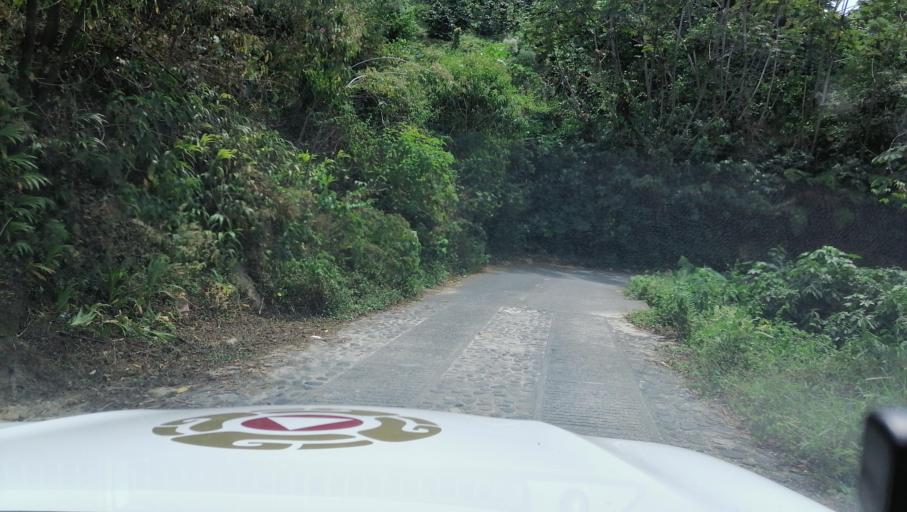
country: MX
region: Chiapas
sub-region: Tapachula
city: Canton Villaflor
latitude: 15.1353
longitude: -92.2890
